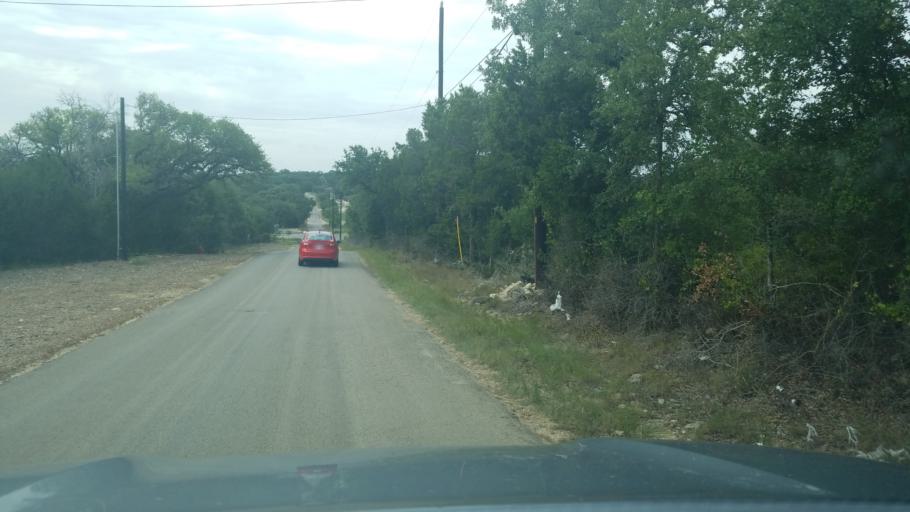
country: US
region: Texas
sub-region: Comal County
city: Bulverde
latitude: 29.7730
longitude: -98.4138
